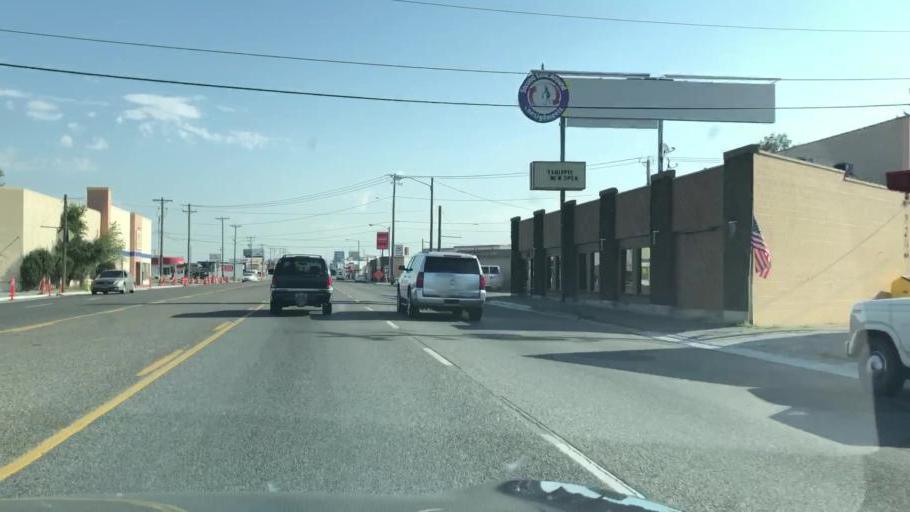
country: US
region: Idaho
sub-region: Bonneville County
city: Idaho Falls
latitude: 43.4982
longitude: -112.0317
